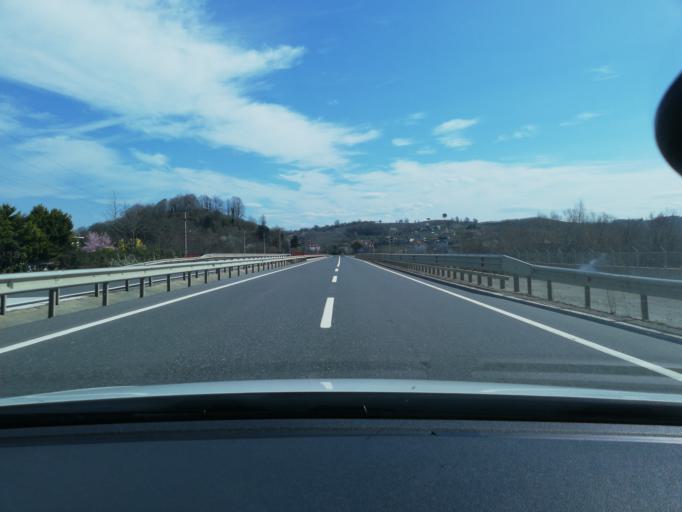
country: TR
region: Duzce
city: Akcakoca
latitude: 41.0966
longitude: 31.2129
